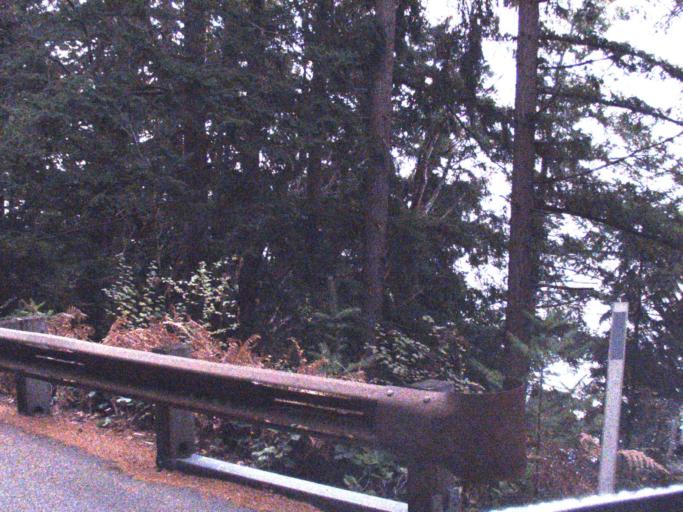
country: US
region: Washington
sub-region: Whatcom County
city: Bellingham
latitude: 48.6405
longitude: -122.4791
